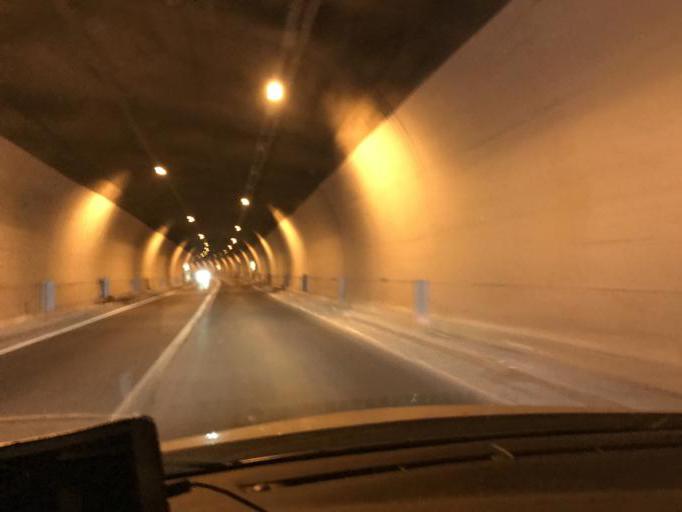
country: IT
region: Latium
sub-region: Provincia di Rieti
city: Colli sul Velino
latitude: 42.5028
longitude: 12.7472
